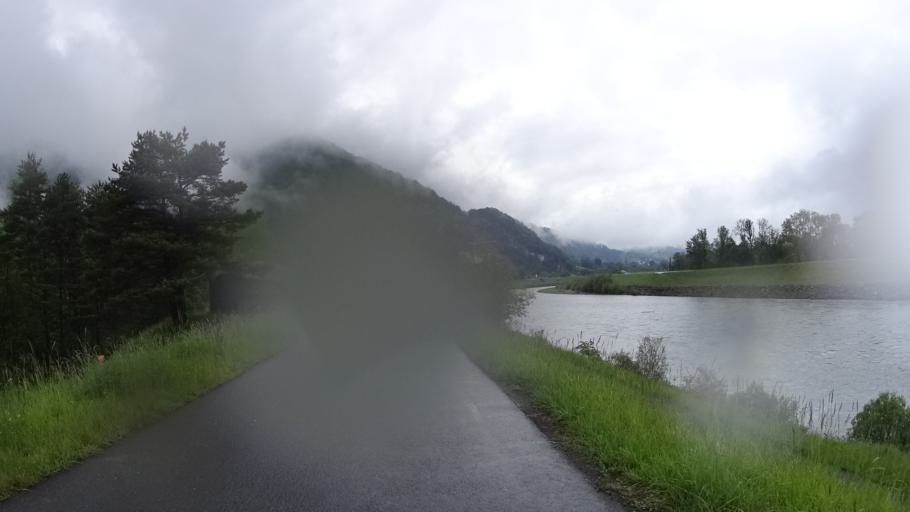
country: LI
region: Balzers
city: Balzers
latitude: 47.0587
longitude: 9.4719
